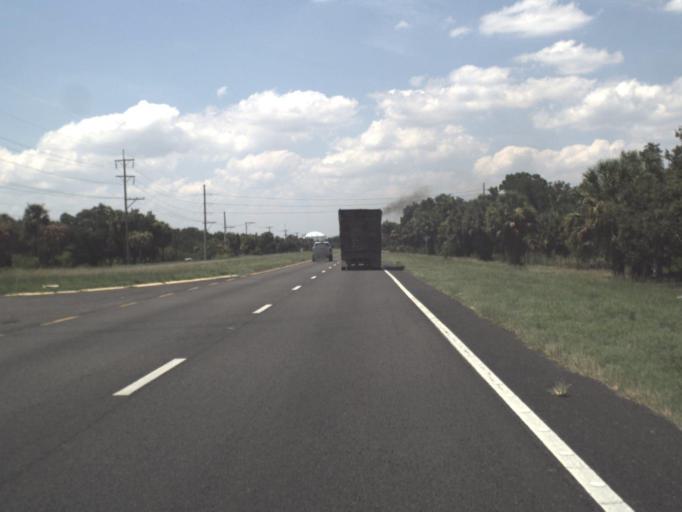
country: US
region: Florida
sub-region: Hillsborough County
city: Gibsonton
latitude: 27.8859
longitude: -82.3974
